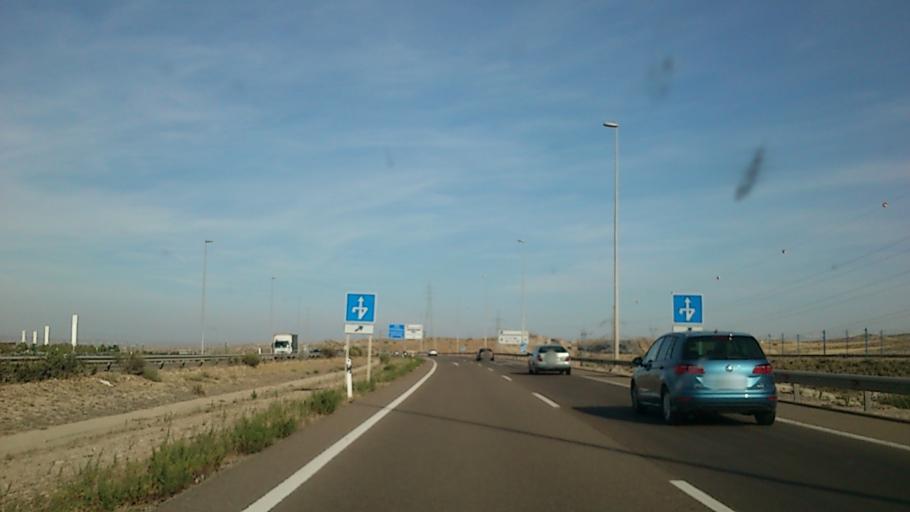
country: ES
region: Aragon
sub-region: Provincia de Zaragoza
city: Cuarte de Huerva
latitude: 41.6050
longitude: -0.8966
